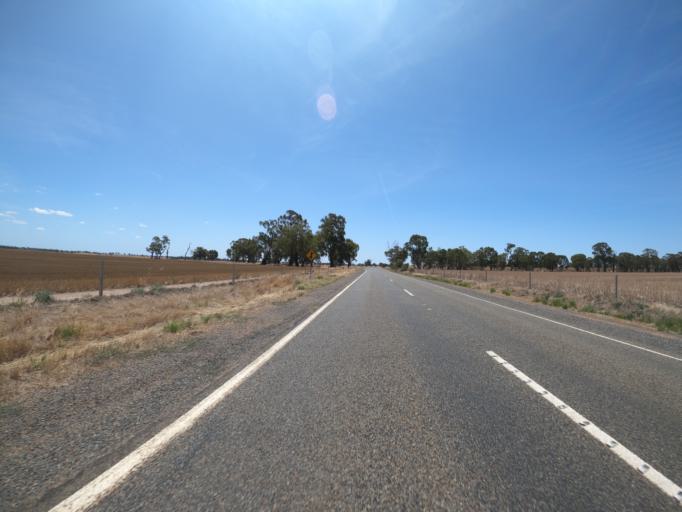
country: AU
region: Victoria
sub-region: Moira
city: Yarrawonga
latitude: -36.1588
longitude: 145.9672
